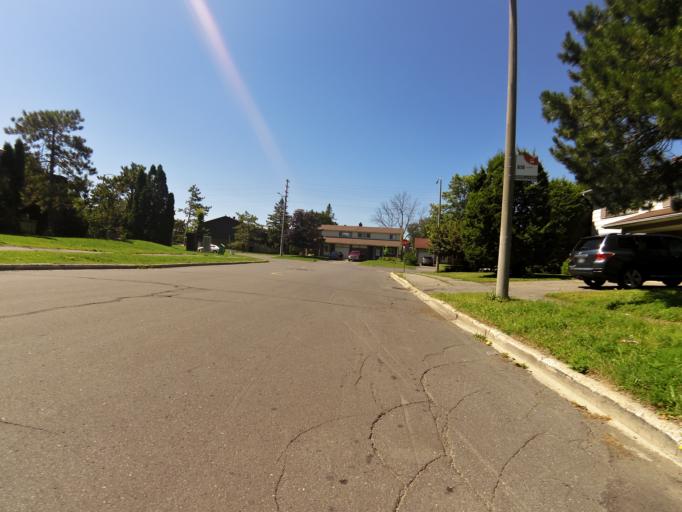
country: CA
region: Ontario
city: Ottawa
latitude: 45.3496
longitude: -75.6621
